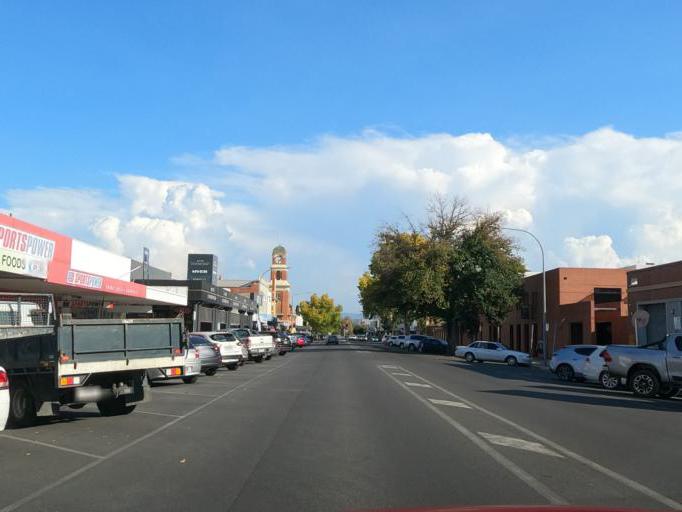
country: AU
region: New South Wales
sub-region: Albury Municipality
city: Albury
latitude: -36.0796
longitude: 146.9185
